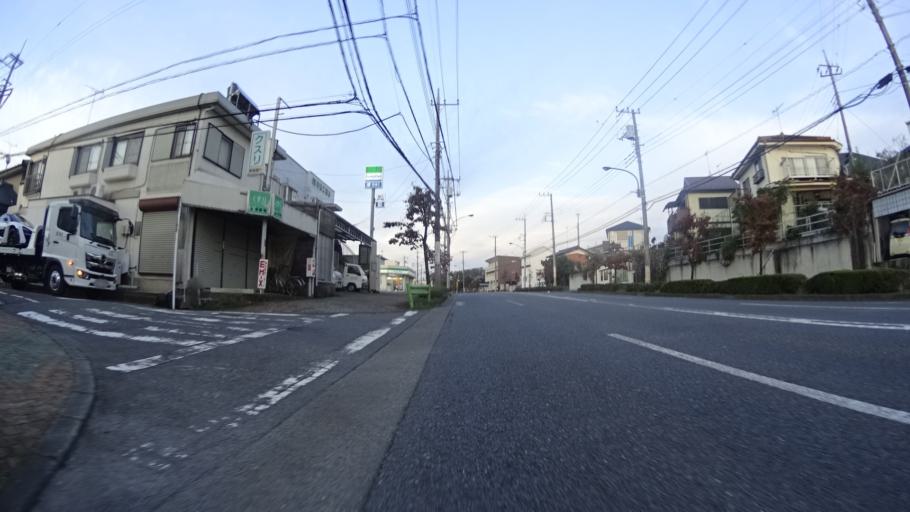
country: JP
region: Tokyo
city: Fussa
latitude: 35.7202
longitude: 139.3219
